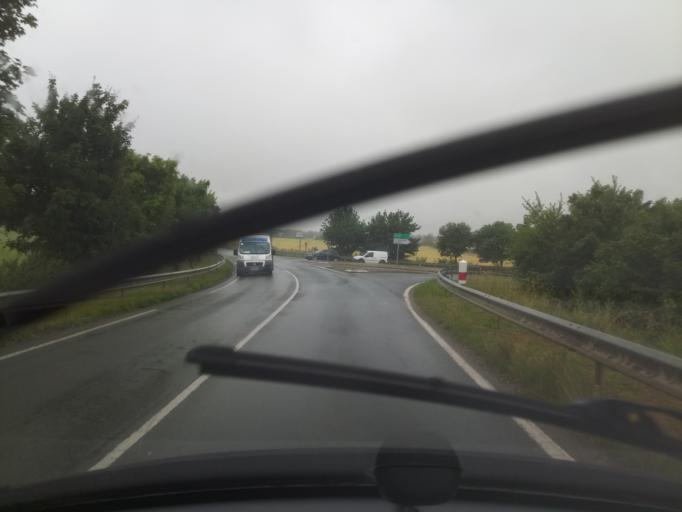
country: FR
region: Poitou-Charentes
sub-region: Departement de la Charente-Maritime
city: Saint-Jean-de-Liversay
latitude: 46.2257
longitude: -0.8787
